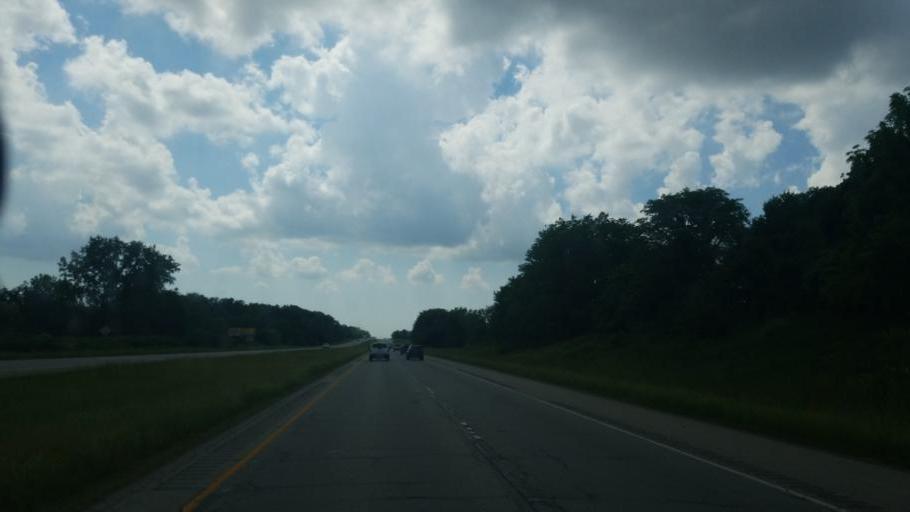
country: US
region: Indiana
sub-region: Kosciusko County
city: Warsaw
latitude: 41.2700
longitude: -85.8855
